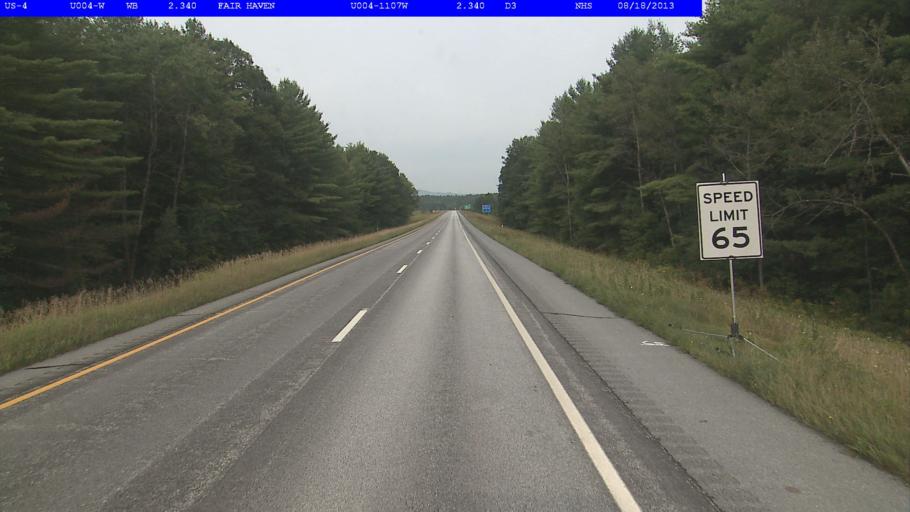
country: US
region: Vermont
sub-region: Rutland County
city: Fair Haven
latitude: 43.6060
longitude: -73.2646
